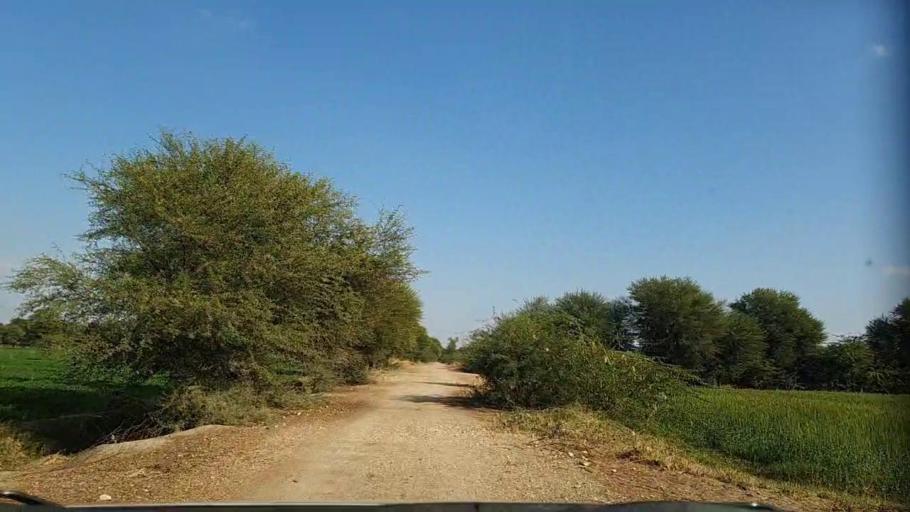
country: PK
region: Sindh
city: Pithoro
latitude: 25.6346
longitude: 69.3587
